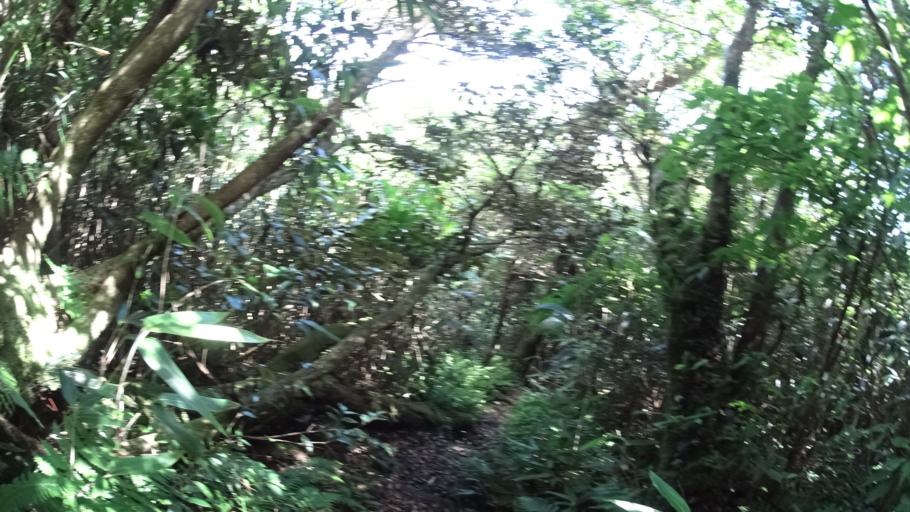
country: JP
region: Shizuoka
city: Shimoda
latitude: 34.5212
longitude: 139.2808
